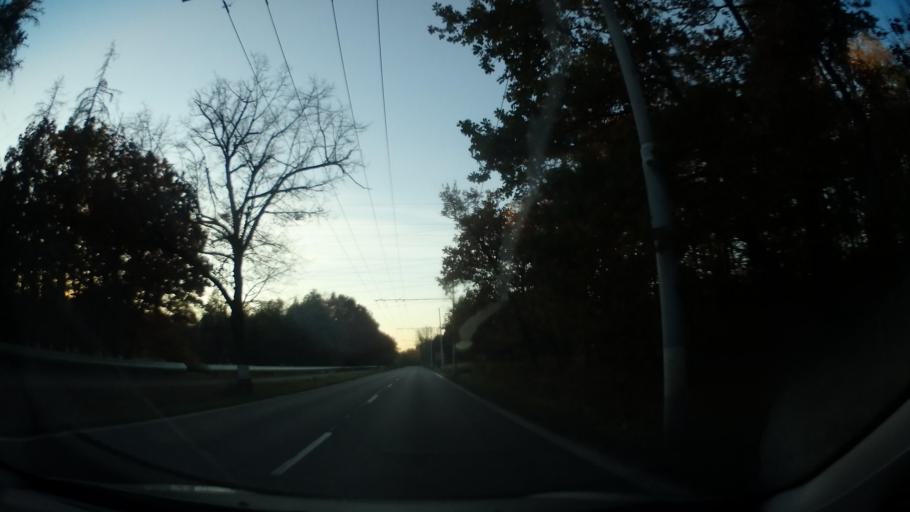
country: CZ
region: Pardubicky
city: Rybitvi
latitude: 50.0692
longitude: 15.6957
